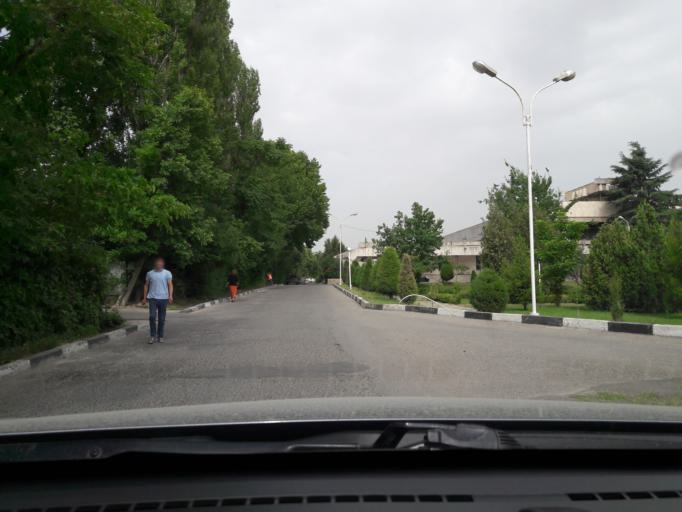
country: TJ
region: Dushanbe
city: Dushanbe
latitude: 38.5817
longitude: 68.7645
